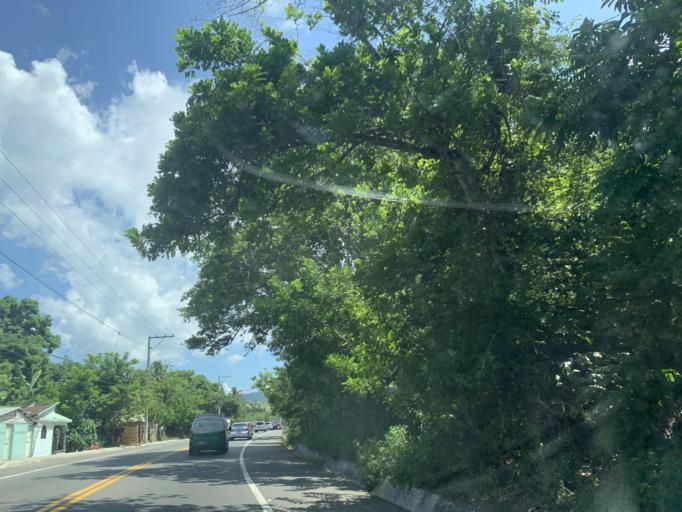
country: DO
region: Puerto Plata
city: Altamira
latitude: 19.6916
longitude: -70.8395
